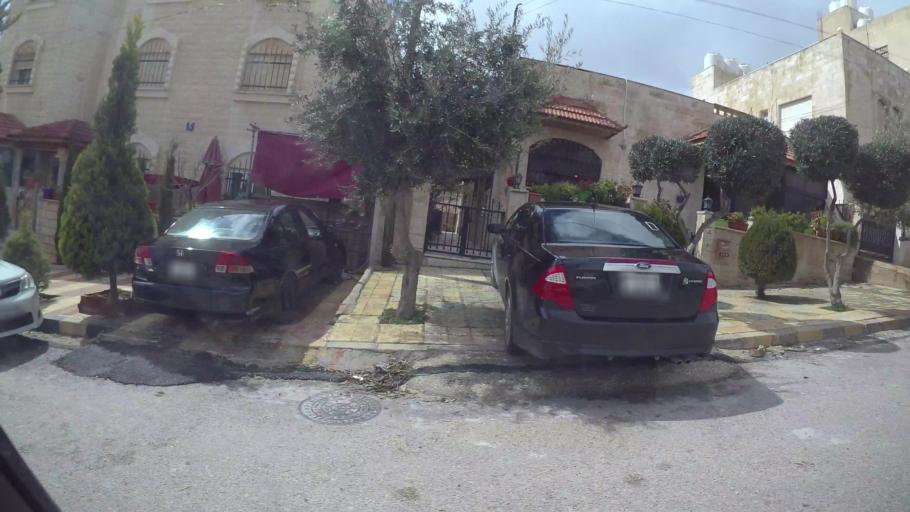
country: JO
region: Amman
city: Al Jubayhah
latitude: 32.0630
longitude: 35.8775
